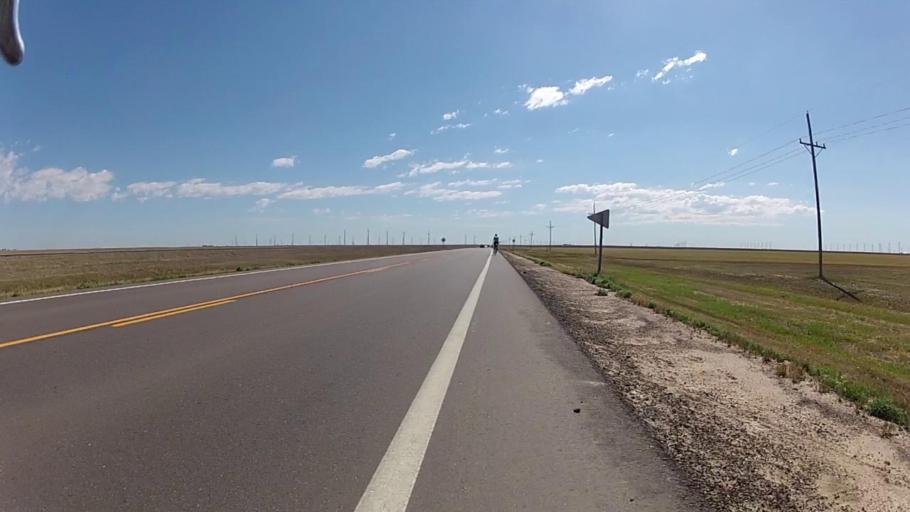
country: US
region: Kansas
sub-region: Gray County
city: Cimarron
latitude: 37.6020
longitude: -100.4323
